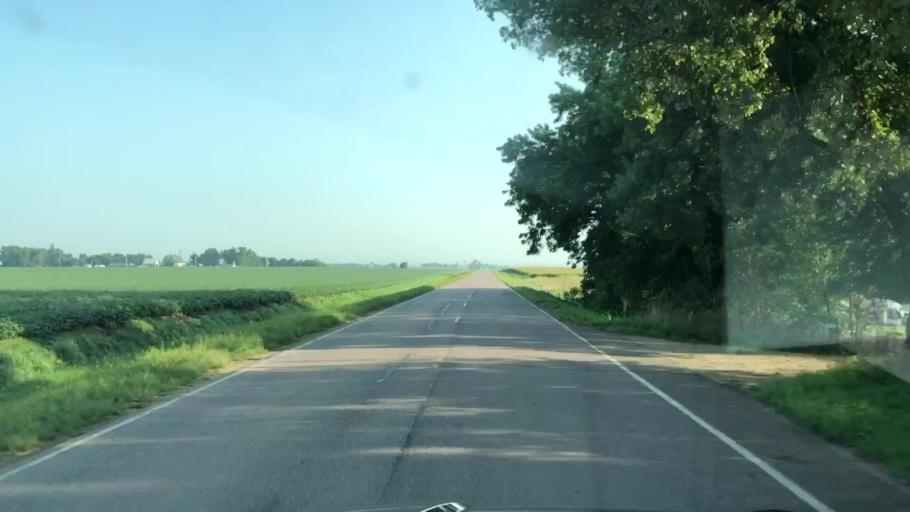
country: US
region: Iowa
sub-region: Sioux County
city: Hull
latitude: 43.2087
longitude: -96.0007
